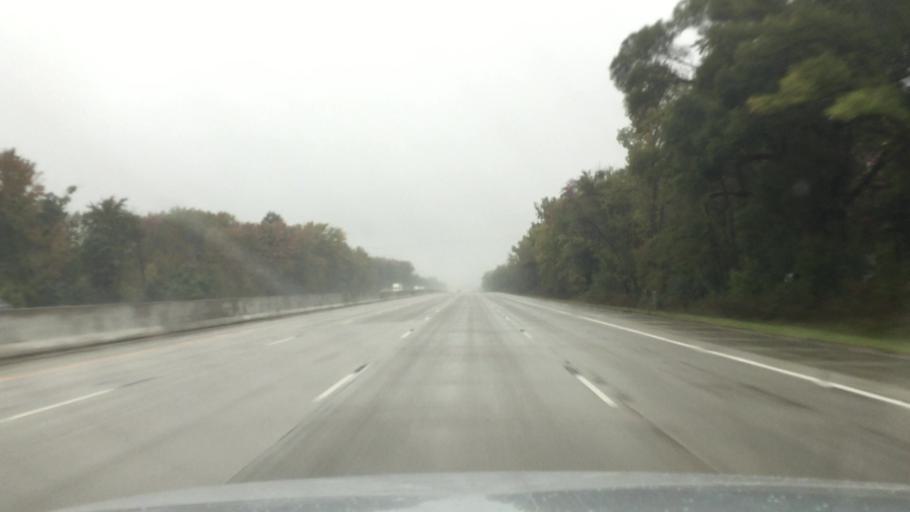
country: US
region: Michigan
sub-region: Saginaw County
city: Bridgeport
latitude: 43.3783
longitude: -83.8759
